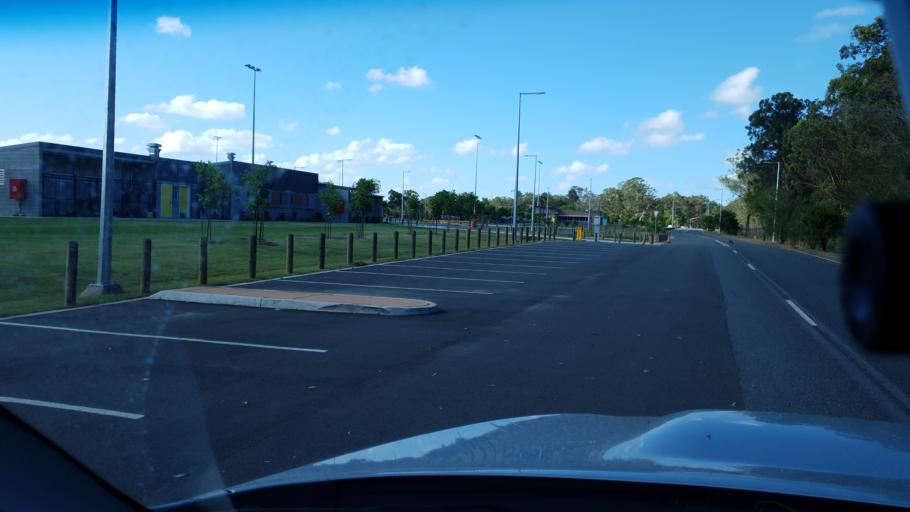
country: AU
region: Queensland
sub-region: Logan
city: Woodridge
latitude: -27.6729
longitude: 153.0703
